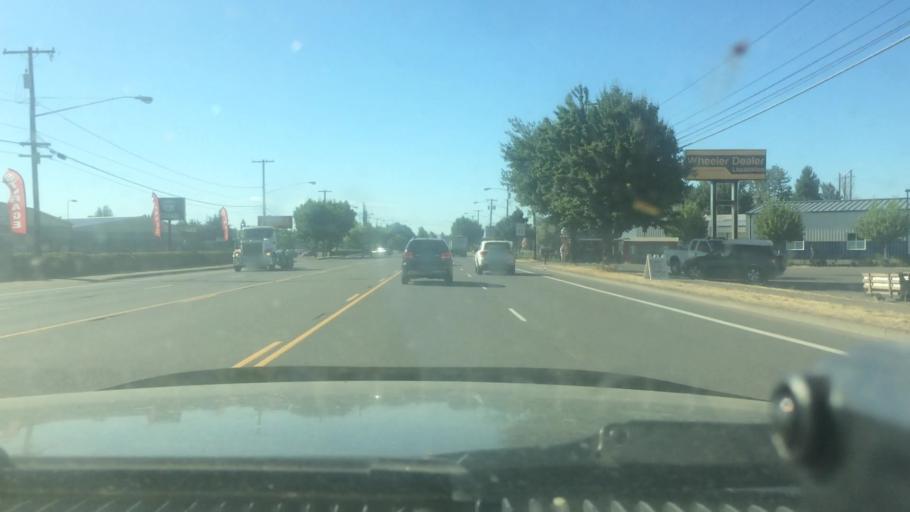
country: US
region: Oregon
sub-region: Lane County
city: Eugene
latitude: 44.0722
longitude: -123.1447
